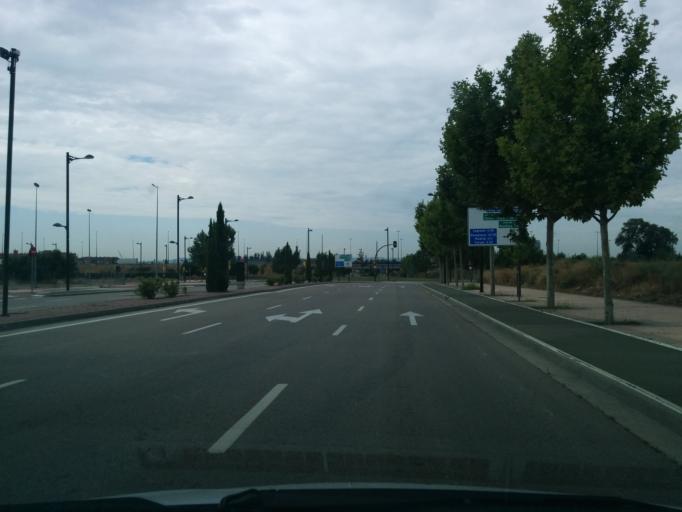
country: ES
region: Aragon
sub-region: Provincia de Zaragoza
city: Almozara
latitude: 41.6829
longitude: -0.8981
